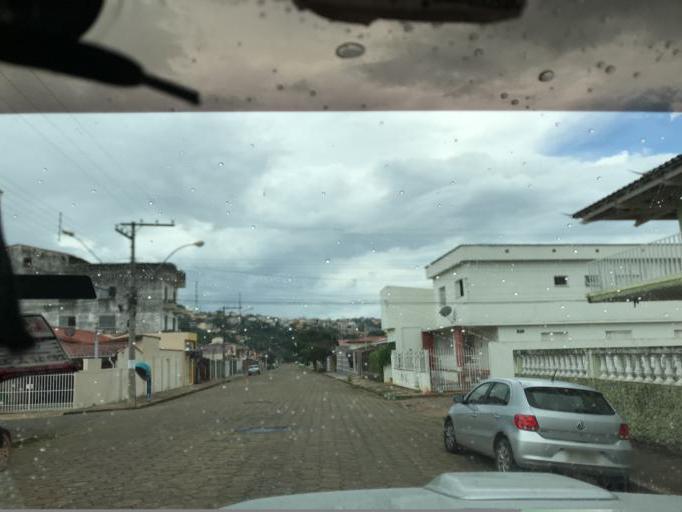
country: BR
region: Minas Gerais
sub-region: Tres Coracoes
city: Tres Coracoes
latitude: -21.7027
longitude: -45.2510
